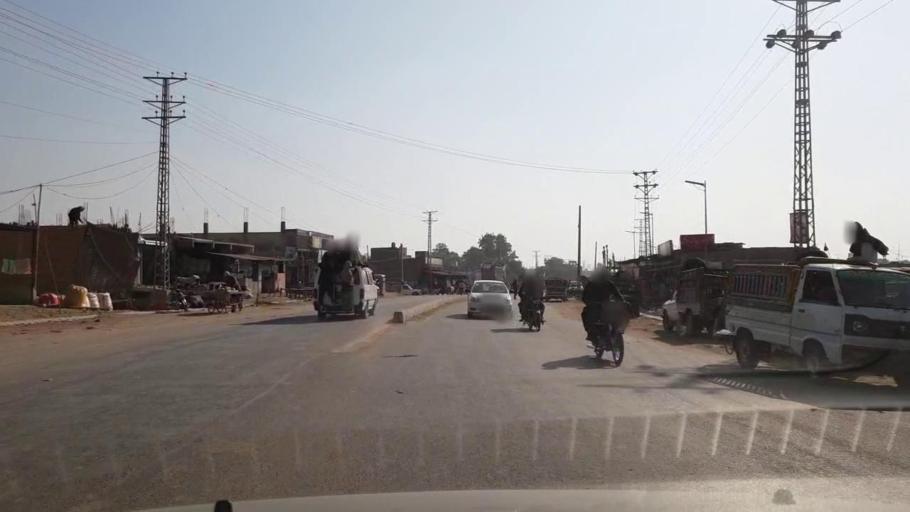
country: PK
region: Sindh
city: Tando Muhammad Khan
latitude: 25.1261
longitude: 68.5449
